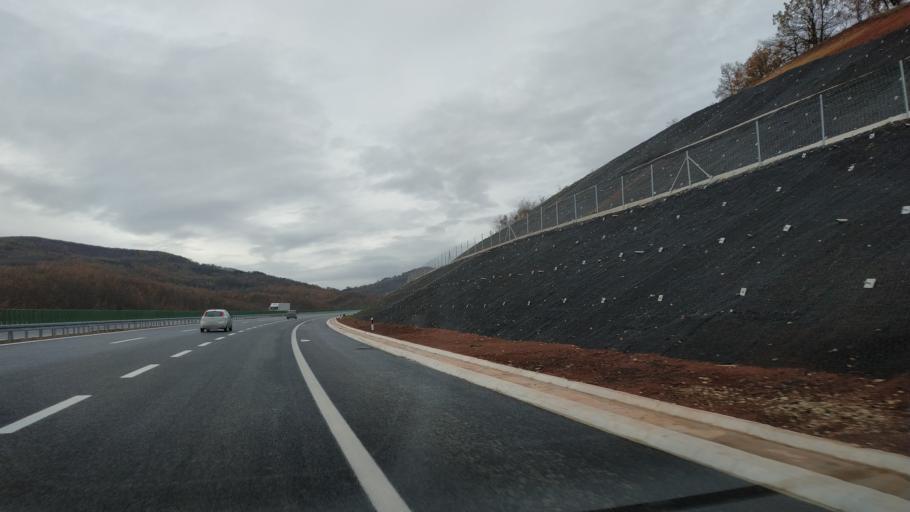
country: RS
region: Central Serbia
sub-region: Nisavski Okrug
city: Gadzin Han
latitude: 43.2582
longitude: 22.1496
